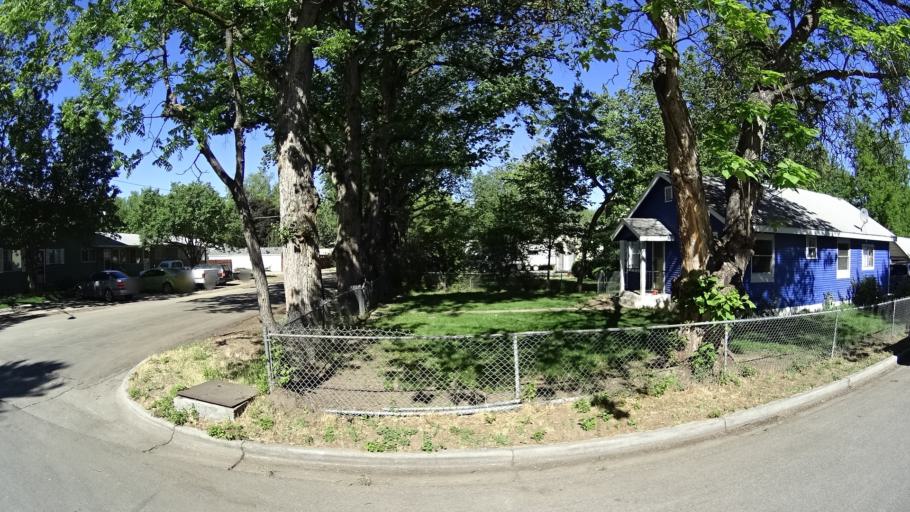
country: US
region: Idaho
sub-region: Ada County
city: Garden City
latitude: 43.6410
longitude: -116.2283
